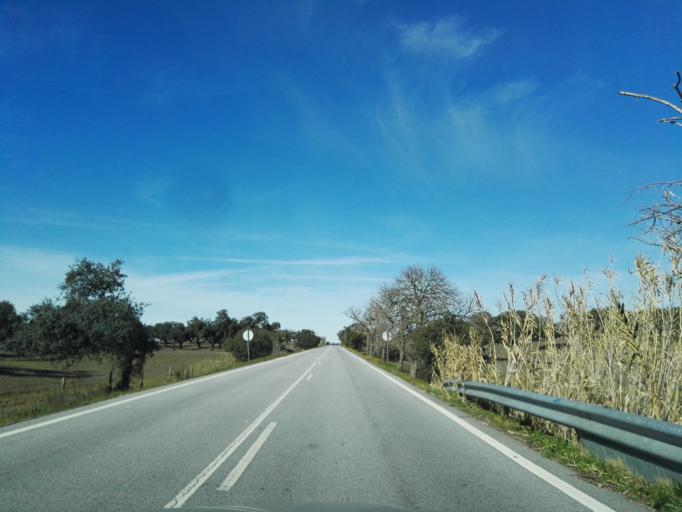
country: PT
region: Portalegre
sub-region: Arronches
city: Arronches
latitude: 39.0759
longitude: -7.2780
